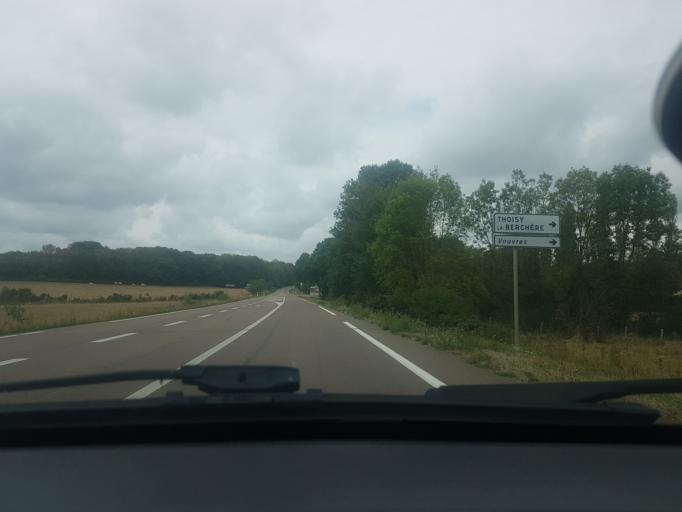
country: FR
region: Bourgogne
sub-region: Departement de la Cote-d'Or
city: Saulieu
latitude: 47.2120
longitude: 4.3561
